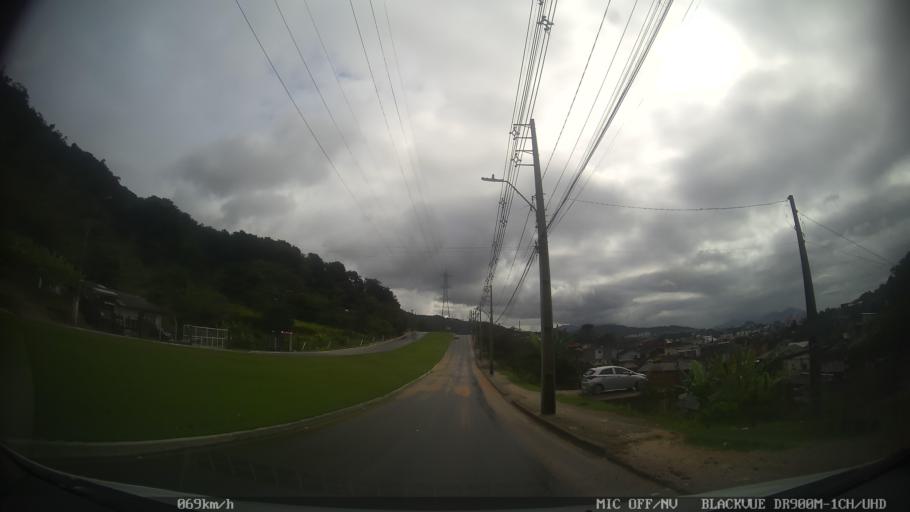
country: BR
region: Santa Catarina
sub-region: Sao Jose
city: Campinas
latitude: -27.5511
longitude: -48.6451
